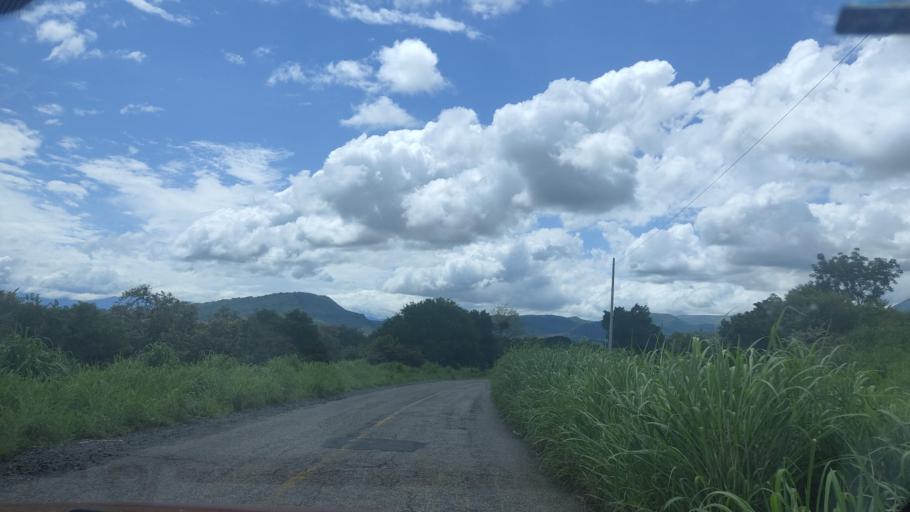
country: MX
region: Nayarit
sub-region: Ahuacatlan
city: Ahuacatlan
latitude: 21.1283
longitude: -104.6061
